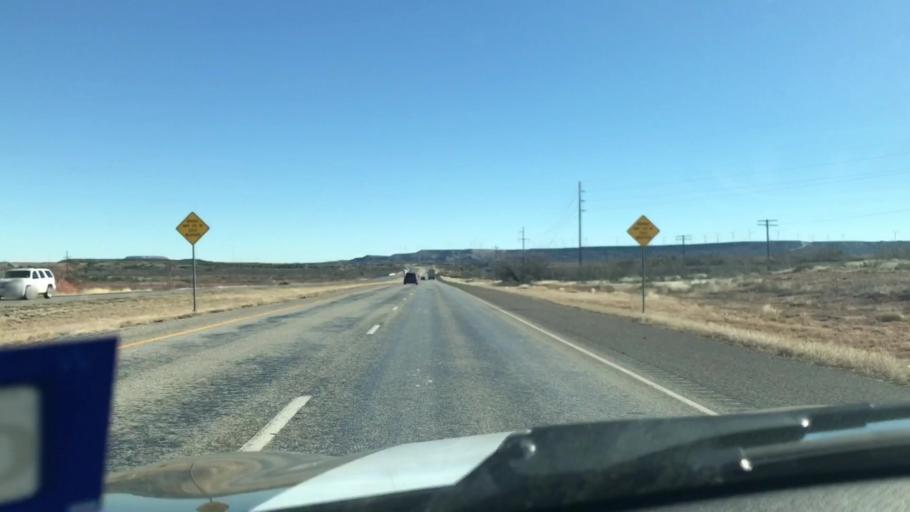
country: US
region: Texas
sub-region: Garza County
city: Post
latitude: 33.0111
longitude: -101.1730
